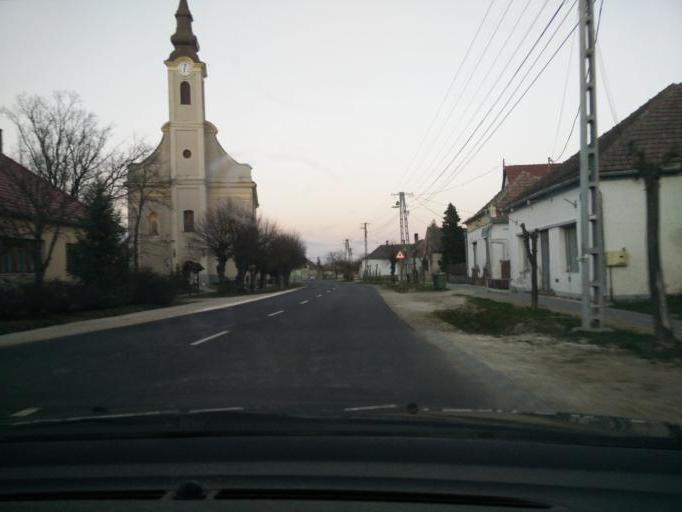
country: HU
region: Veszprem
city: Csabrendek
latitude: 47.0654
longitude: 17.3438
